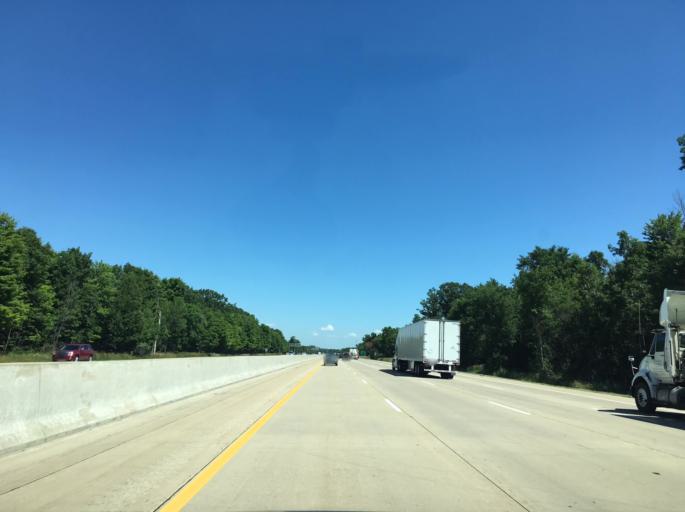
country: US
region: Michigan
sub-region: Genesee County
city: Clio
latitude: 43.1289
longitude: -83.7634
